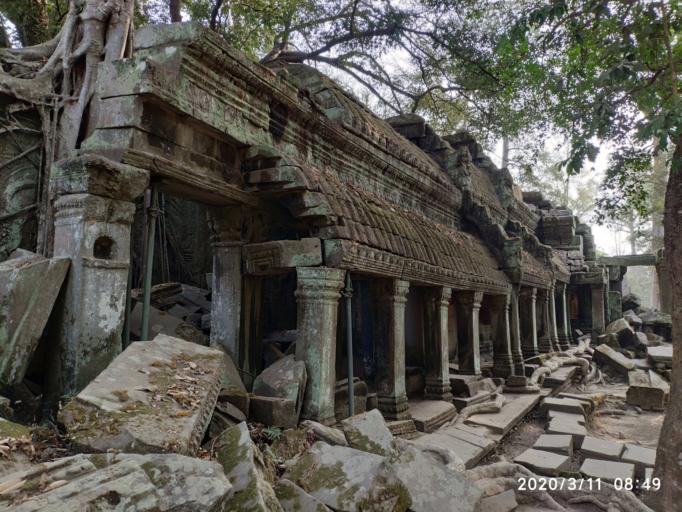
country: KH
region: Siem Reap
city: Siem Reap
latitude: 13.4343
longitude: 103.8891
